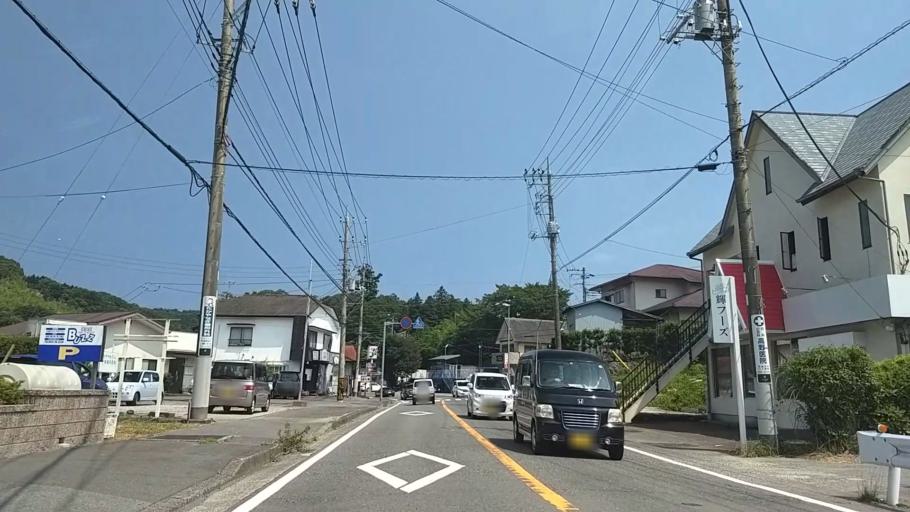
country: JP
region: Shizuoka
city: Ito
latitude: 34.9362
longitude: 139.0889
